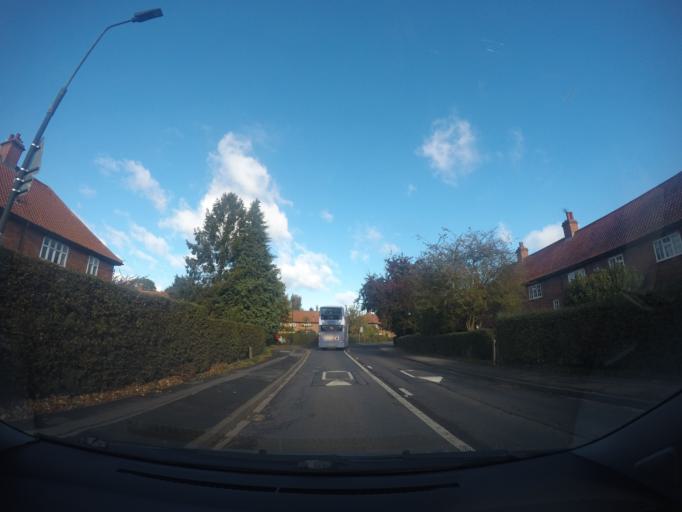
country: GB
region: England
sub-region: City of York
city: Haxby
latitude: 53.9930
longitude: -1.0725
